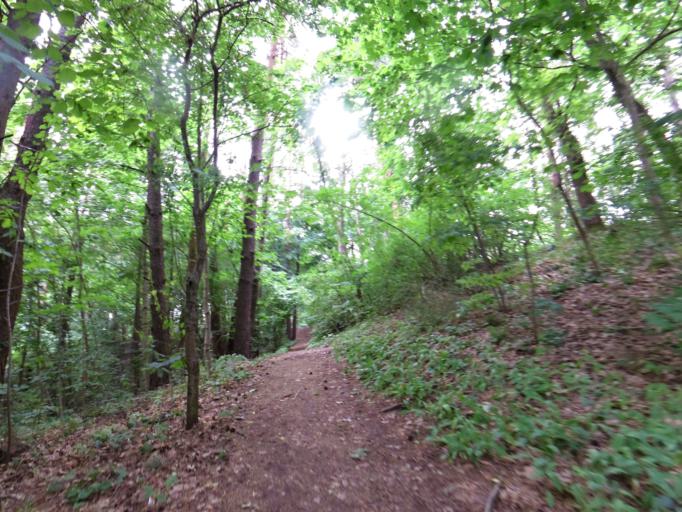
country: LT
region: Vilnius County
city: Lazdynai
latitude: 54.6857
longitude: 25.2167
